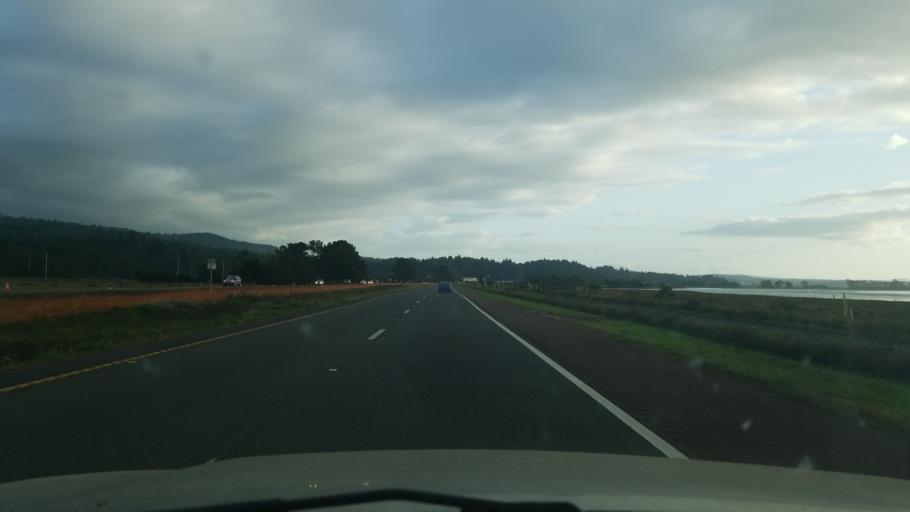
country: US
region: California
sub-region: Humboldt County
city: Bayside
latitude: 40.8392
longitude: -124.0822
